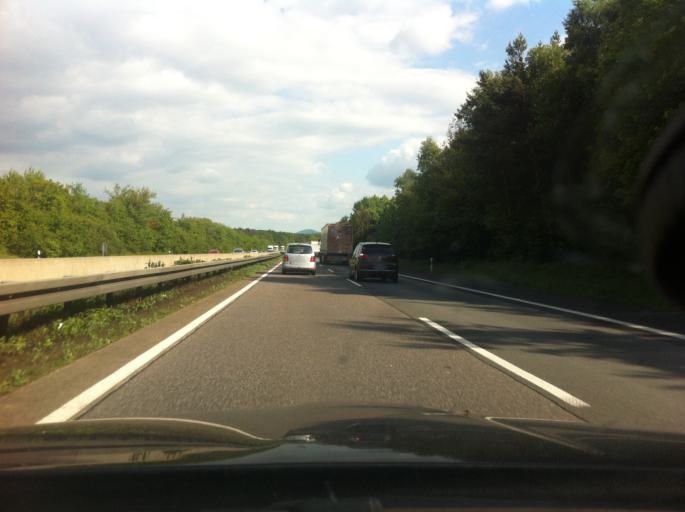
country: DE
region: Hesse
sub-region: Regierungsbezirk Kassel
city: Volkmarsen
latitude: 51.4443
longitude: 9.1404
